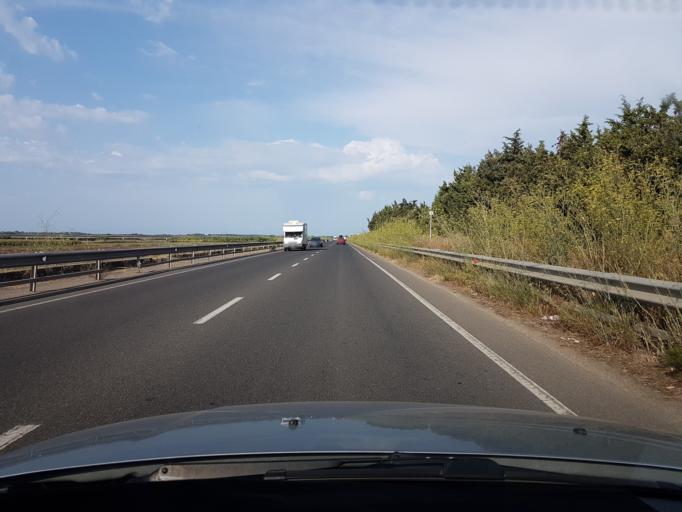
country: IT
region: Sardinia
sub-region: Provincia di Oristano
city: Solanas
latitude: 39.9197
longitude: 8.5605
